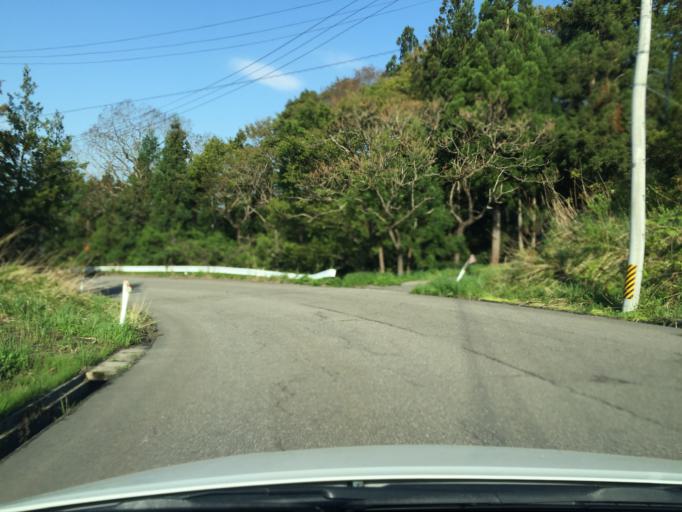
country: JP
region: Fukushima
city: Kitakata
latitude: 37.6839
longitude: 139.6841
